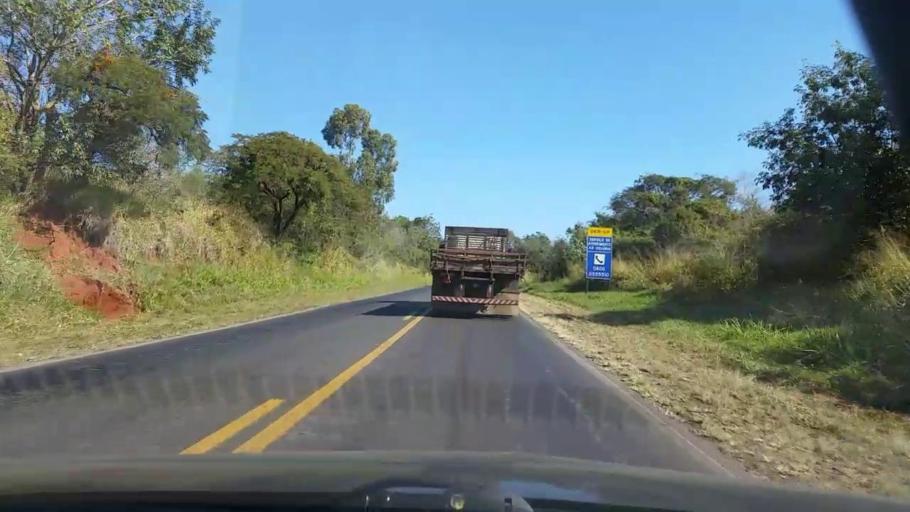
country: BR
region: Sao Paulo
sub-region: Sao Manuel
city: Sao Manuel
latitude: -22.8112
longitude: -48.6769
